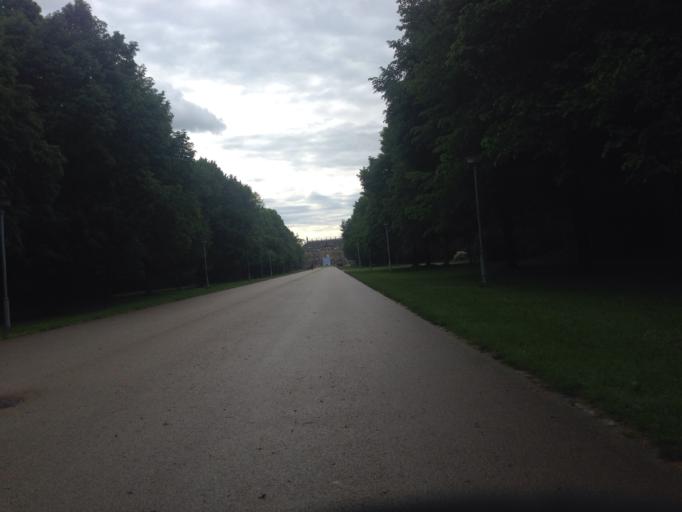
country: DE
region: Saxony
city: Dresden
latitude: 51.0404
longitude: 13.7563
